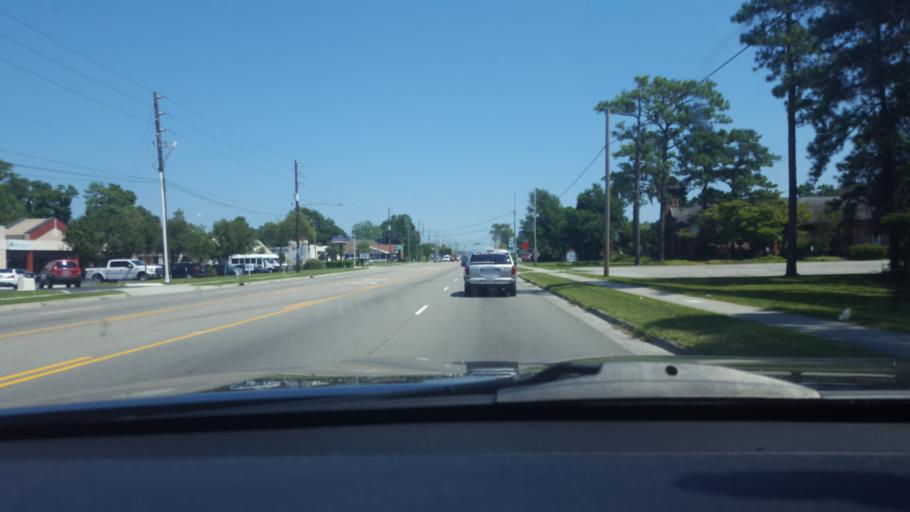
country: US
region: North Carolina
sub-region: New Hanover County
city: Kings Grant
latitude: 34.2412
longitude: -77.8991
